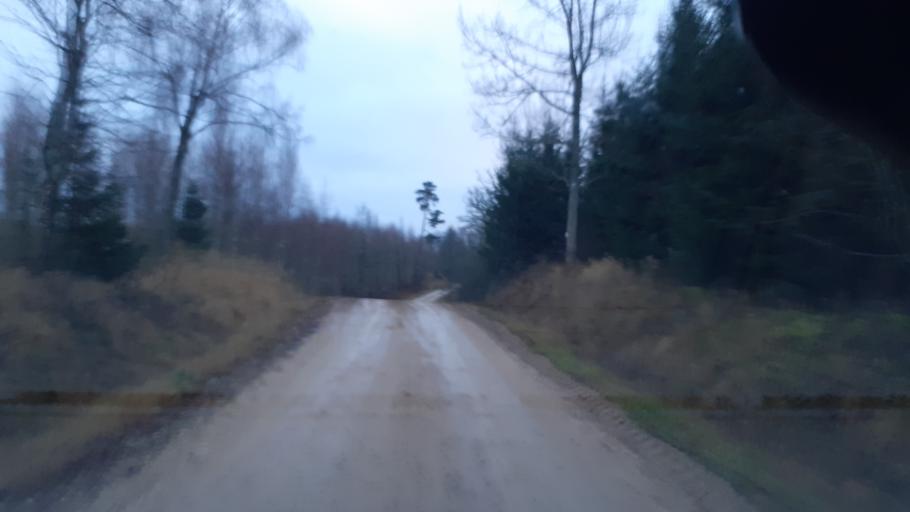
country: LV
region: Alsunga
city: Alsunga
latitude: 56.9101
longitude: 21.7127
